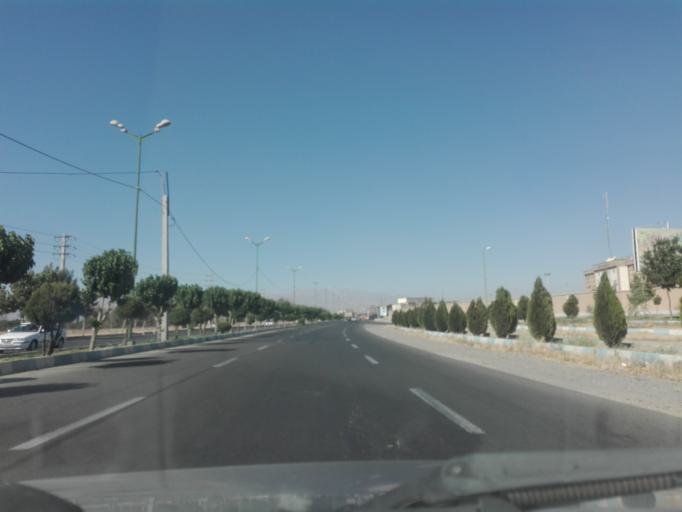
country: IR
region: Tehran
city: Shahriar
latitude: 35.6323
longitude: 51.0580
